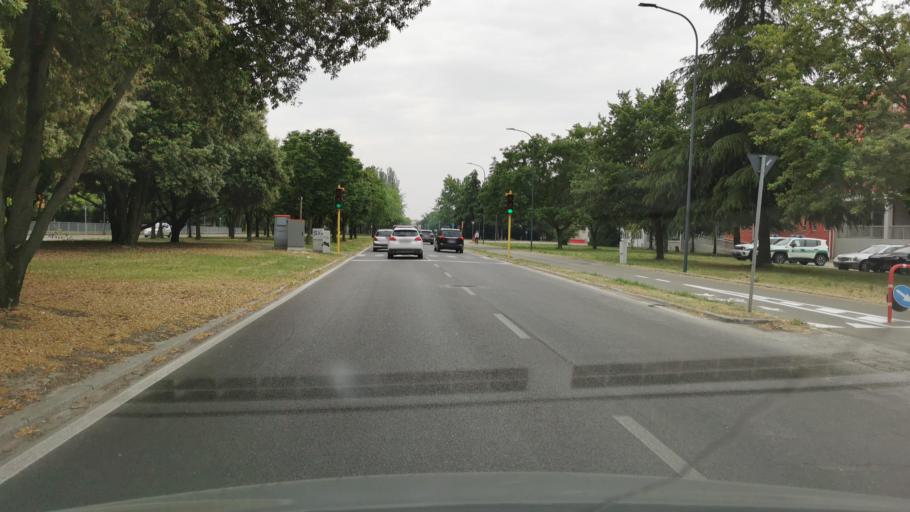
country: IT
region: Emilia-Romagna
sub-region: Provincia di Ravenna
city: Ravenna
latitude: 44.4085
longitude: 12.1904
